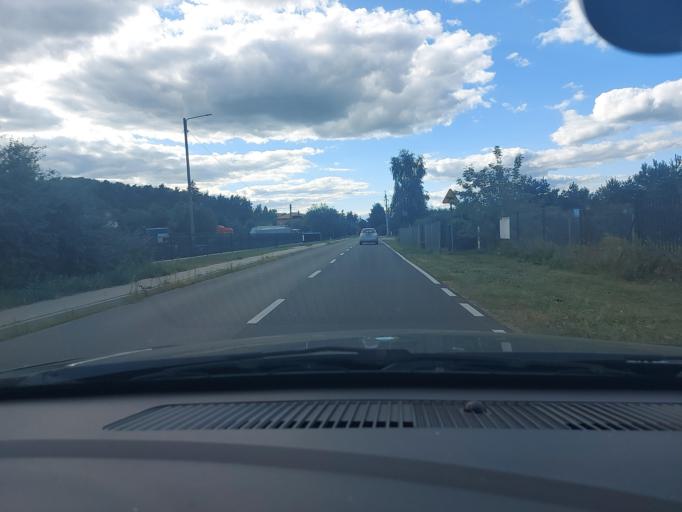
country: PL
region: Masovian Voivodeship
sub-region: Powiat nowodworski
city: Pomiechowek
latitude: 52.4884
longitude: 20.7127
